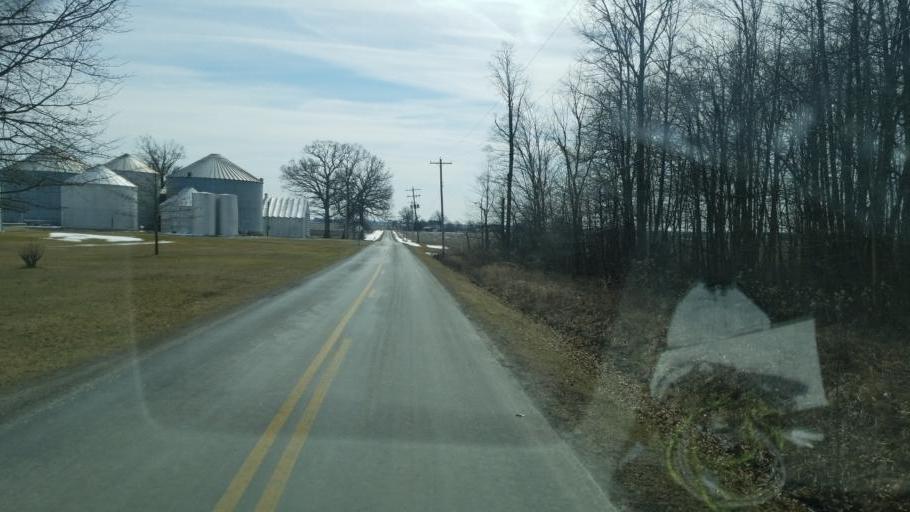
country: US
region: Ohio
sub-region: Delaware County
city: Delaware
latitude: 40.3388
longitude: -82.9978
